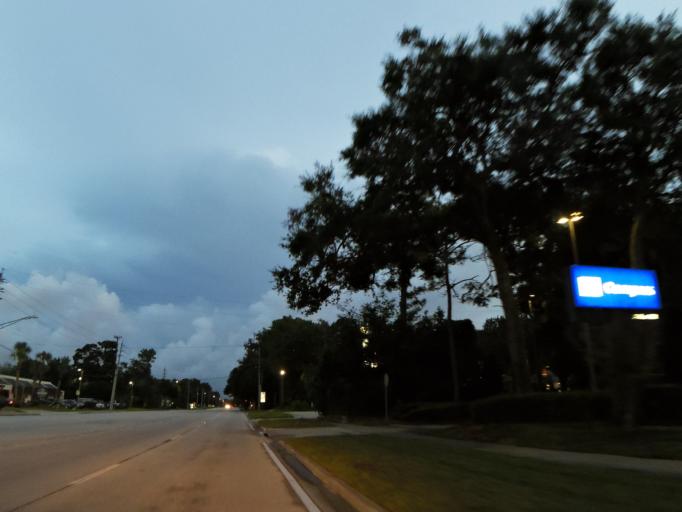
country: US
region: Florida
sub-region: Duval County
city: Jacksonville
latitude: 30.3636
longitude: -81.6068
